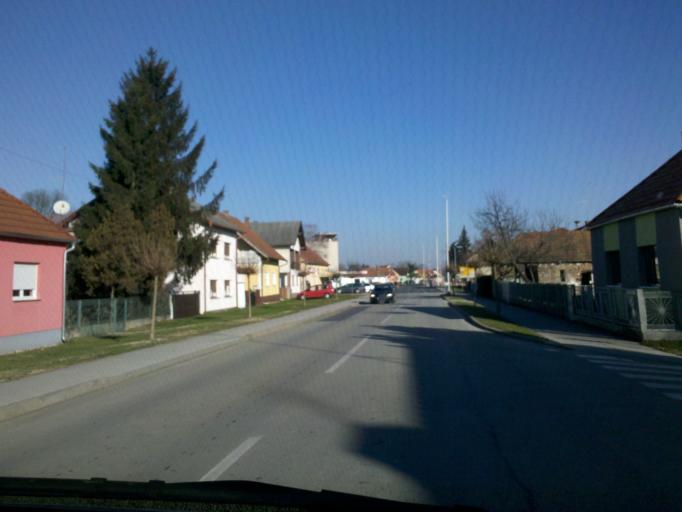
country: HR
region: Medimurska
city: Kotoriba
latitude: 46.3520
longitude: 16.8116
